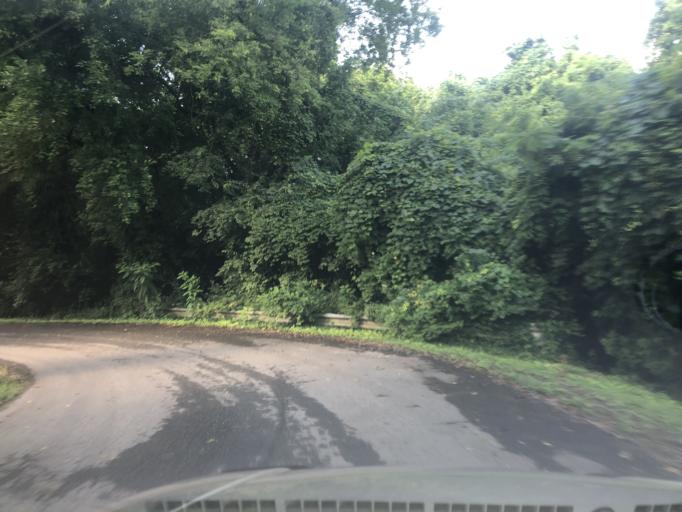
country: US
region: Tennessee
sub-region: Davidson County
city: Lakewood
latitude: 36.2429
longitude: -86.7152
